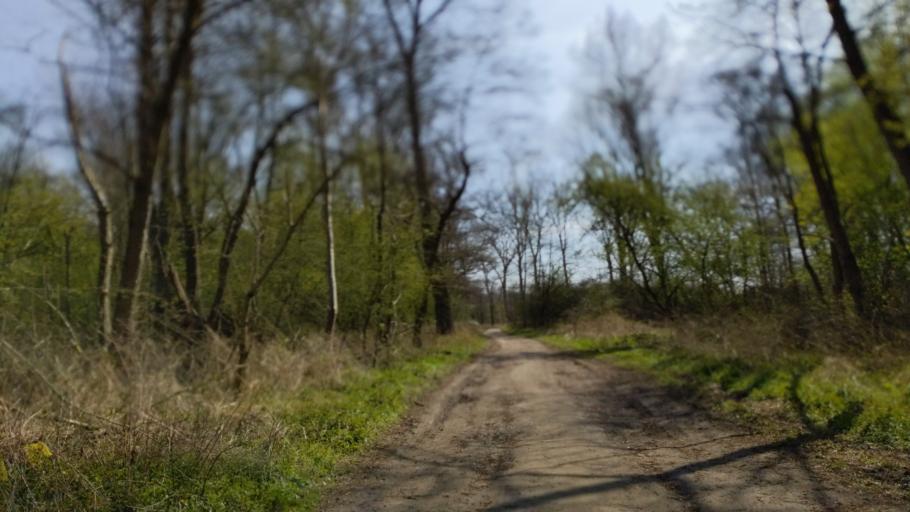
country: DE
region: Schleswig-Holstein
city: Travemuende
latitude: 53.9514
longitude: 10.8766
